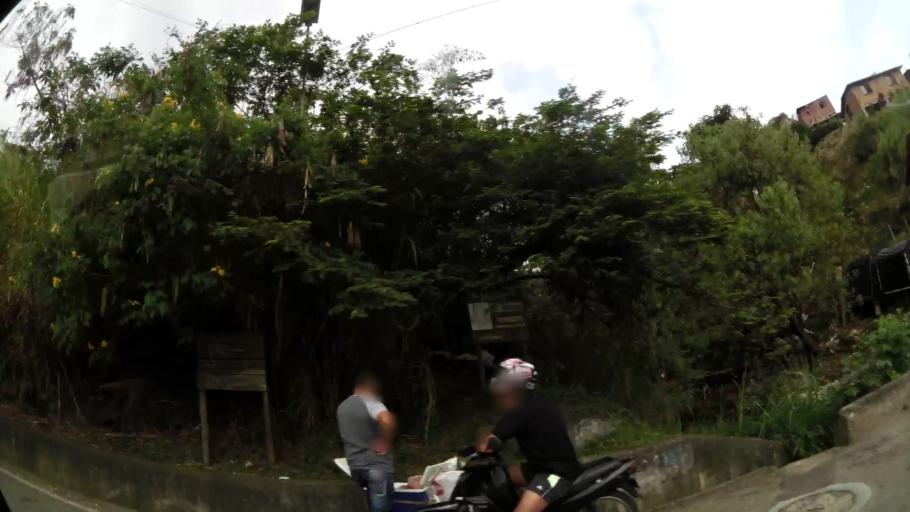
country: CO
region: Antioquia
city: Medellin
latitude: 6.2794
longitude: -75.6091
